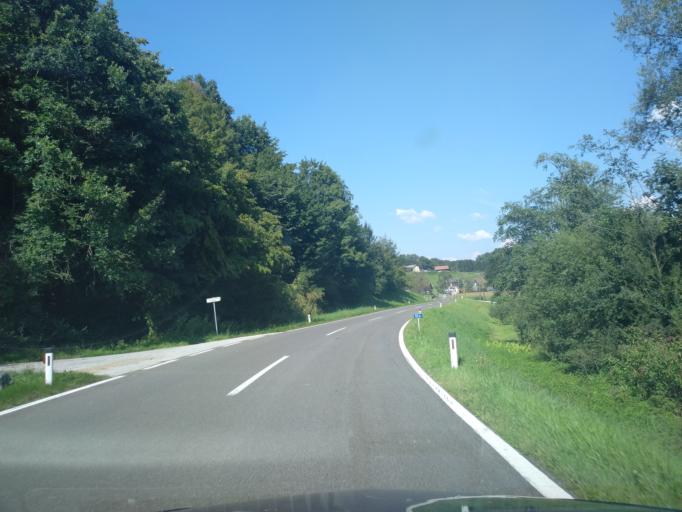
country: AT
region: Styria
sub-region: Politischer Bezirk Leibnitz
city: Gamlitz
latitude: 46.7107
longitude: 15.5066
